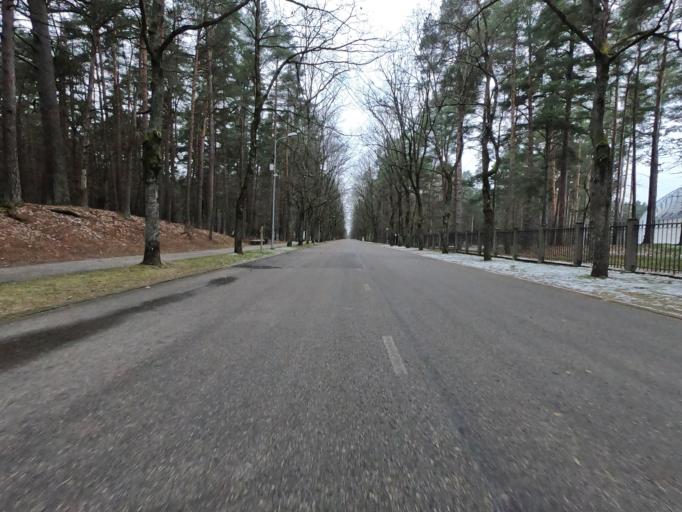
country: LV
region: Riga
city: Jaunciems
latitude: 57.0137
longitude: 24.1510
